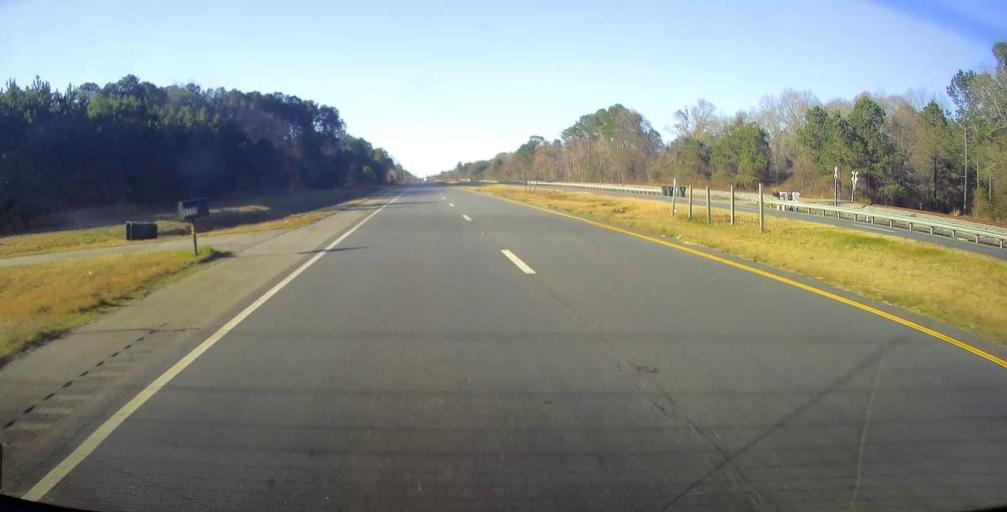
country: US
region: Georgia
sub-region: Lee County
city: Leesburg
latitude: 31.8358
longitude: -84.2213
